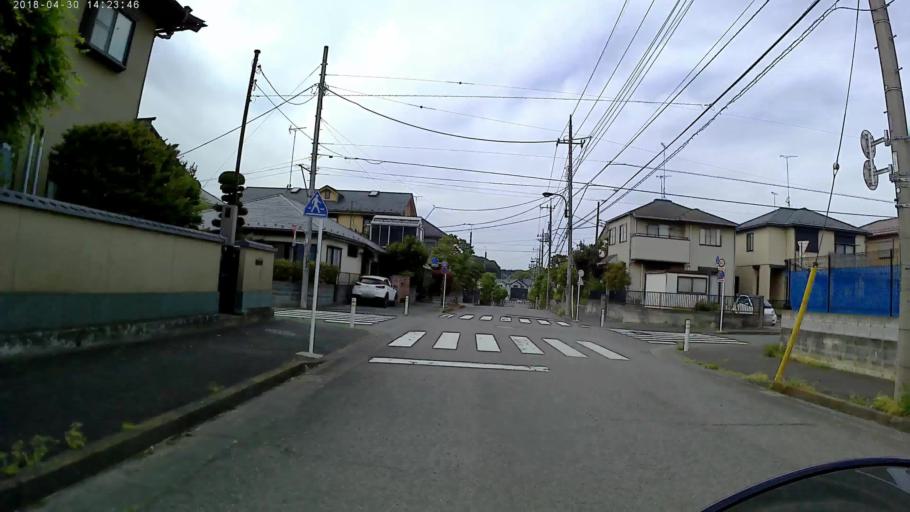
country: JP
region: Tokyo
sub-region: Machida-shi
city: Machida
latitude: 35.5722
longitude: 139.4113
